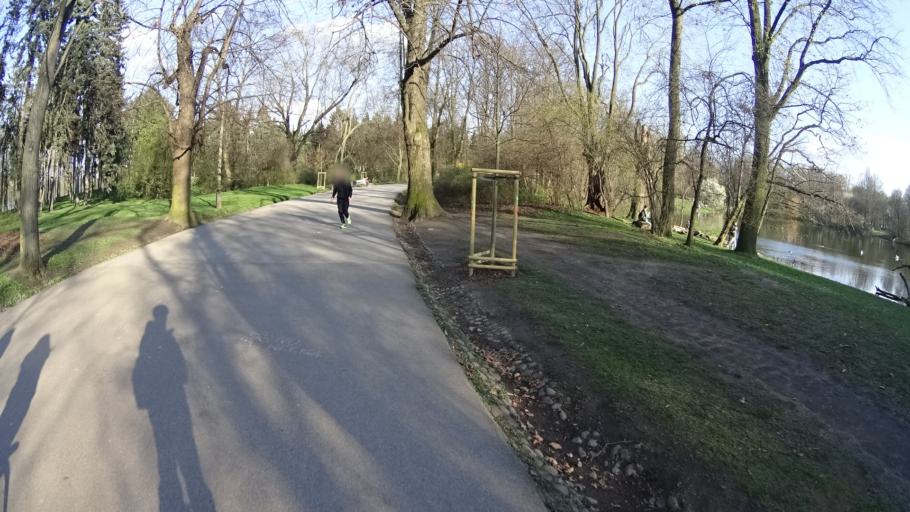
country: PL
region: Masovian Voivodeship
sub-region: Warszawa
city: Praga Polnoc
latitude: 52.2428
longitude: 21.0577
